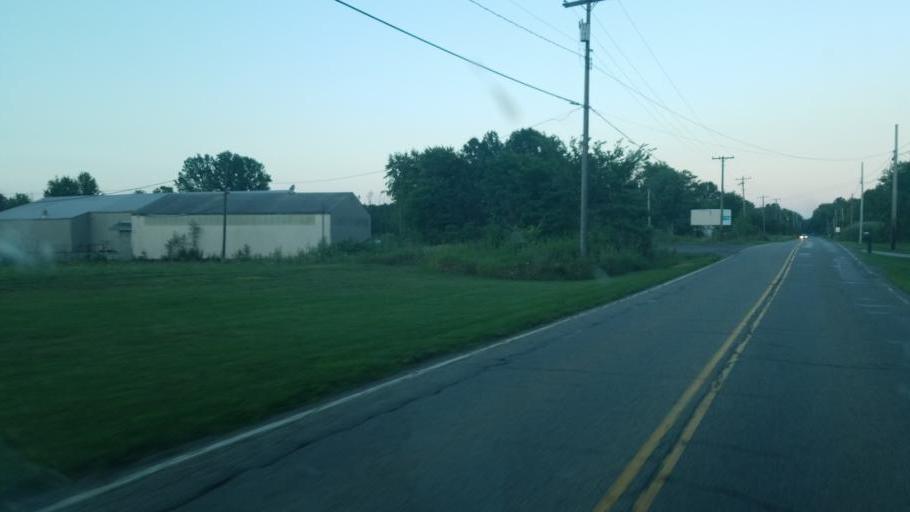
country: US
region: Ohio
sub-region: Trumbull County
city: Champion Heights
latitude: 41.3003
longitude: -80.8976
